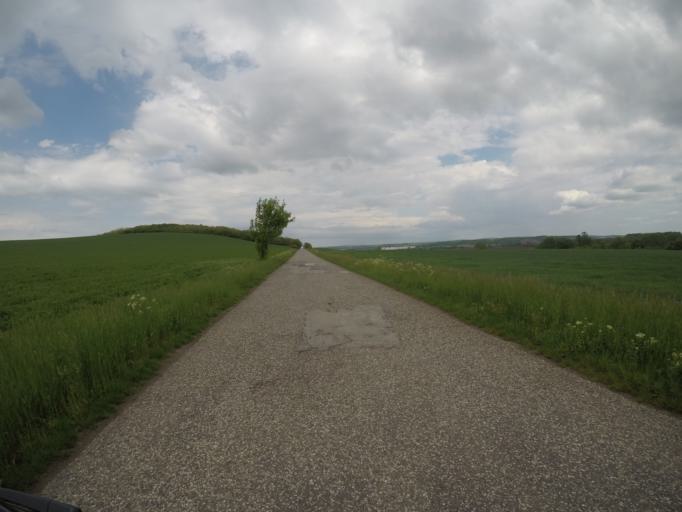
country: SK
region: Nitriansky
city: Sahy
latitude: 48.0821
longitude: 18.8655
